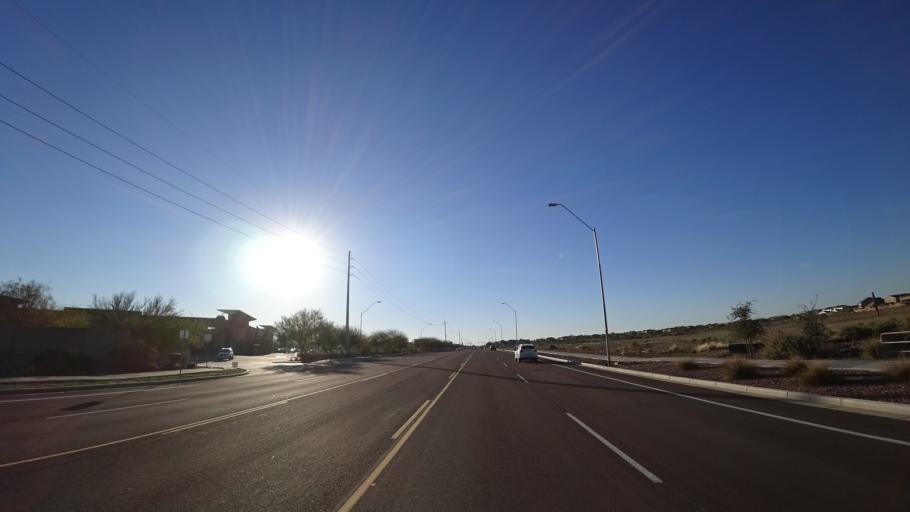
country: US
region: Arizona
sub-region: Maricopa County
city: Sun City West
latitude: 33.6817
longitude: -112.2751
